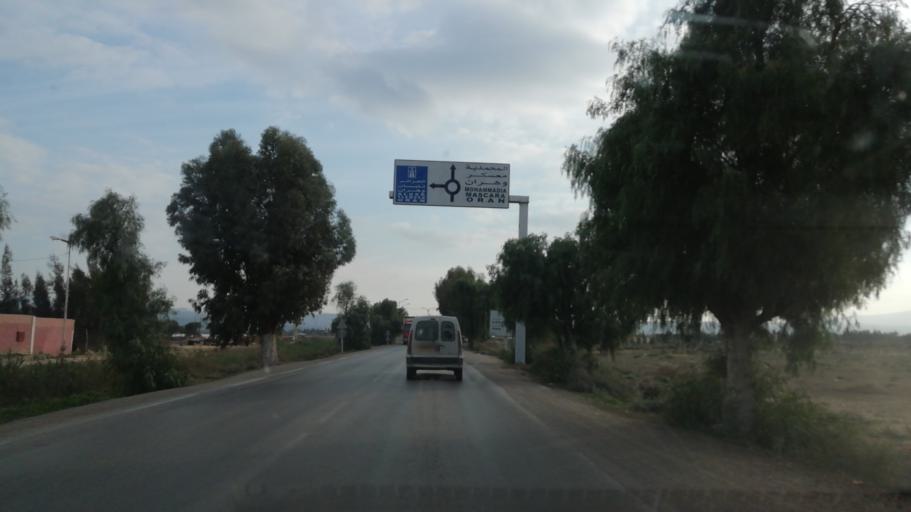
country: DZ
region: Mascara
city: Mascara
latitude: 35.6308
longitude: 0.0612
